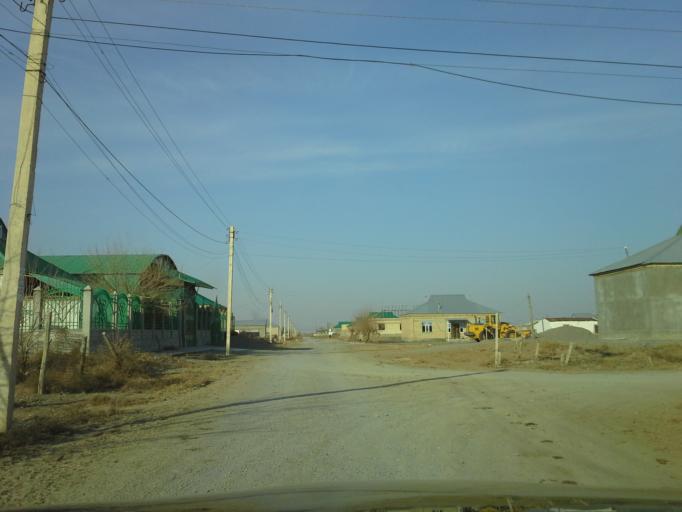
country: TM
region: Ahal
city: Abadan
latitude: 38.1754
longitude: 58.0466
